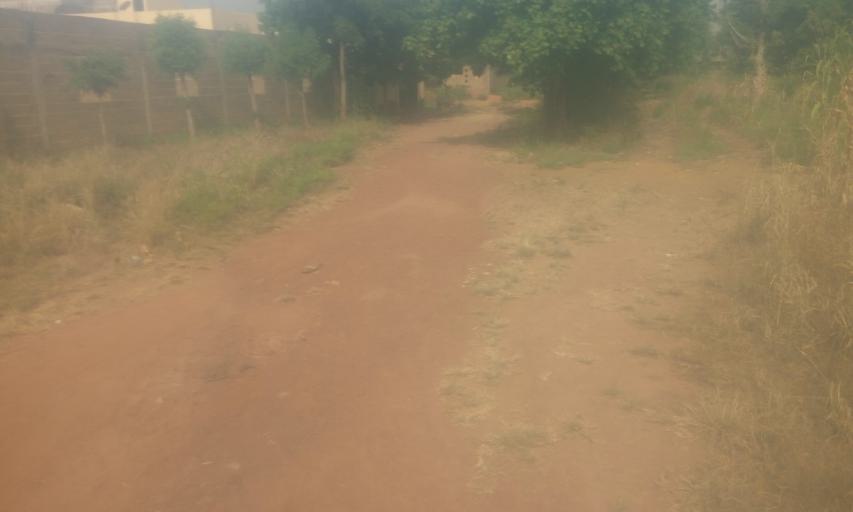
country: ML
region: Bamako
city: Bamako
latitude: 12.5782
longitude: -8.0794
